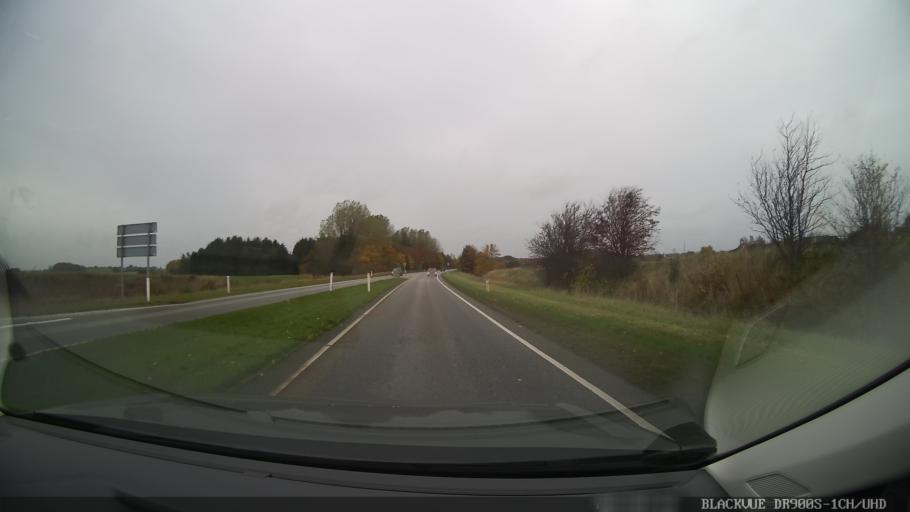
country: DK
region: North Denmark
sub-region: Thisted Kommune
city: Thisted
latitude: 56.8306
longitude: 8.7121
